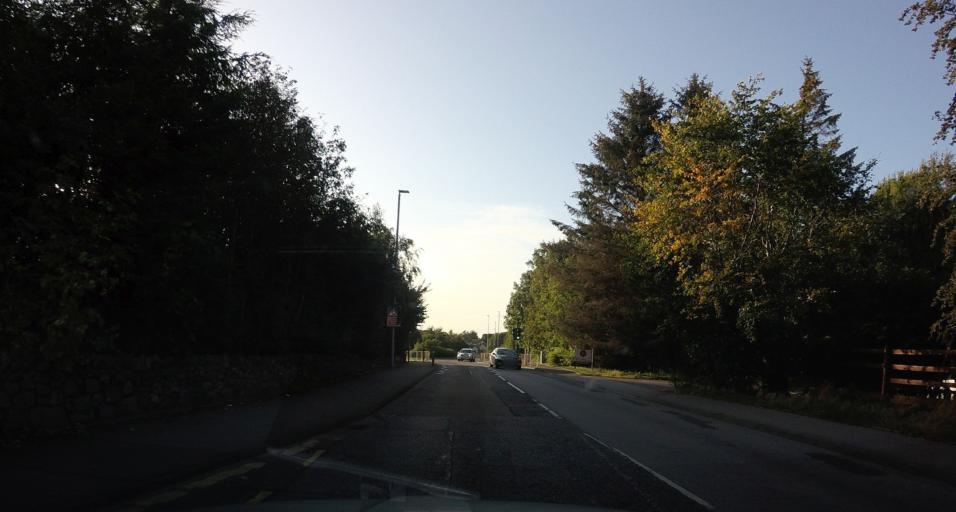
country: GB
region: Scotland
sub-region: Aberdeenshire
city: Westhill
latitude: 57.1506
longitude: -2.3014
